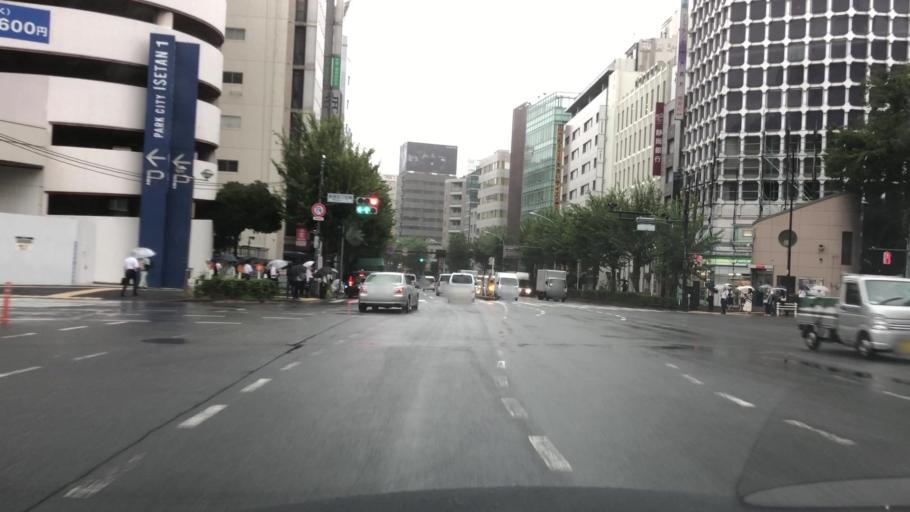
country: JP
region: Tokyo
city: Tokyo
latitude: 35.6922
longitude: 139.7068
